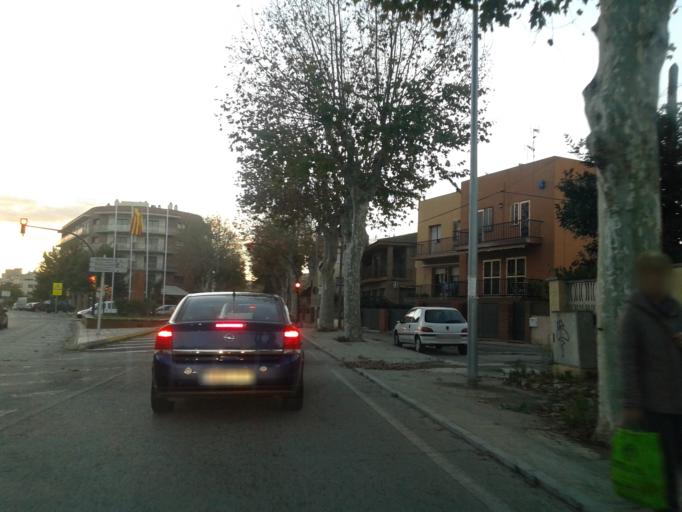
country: ES
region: Catalonia
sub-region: Provincia de Tarragona
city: Torredembarra
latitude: 41.1463
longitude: 1.4100
